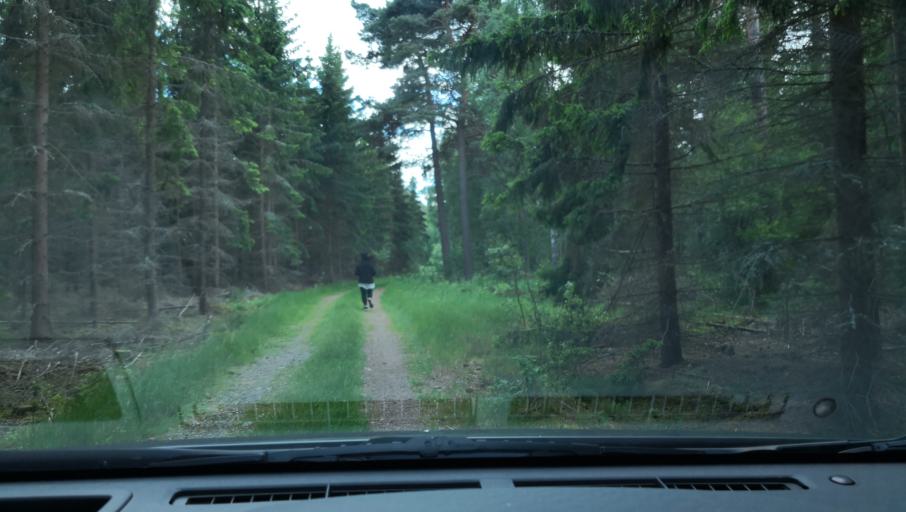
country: SE
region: OErebro
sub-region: Lindesbergs Kommun
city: Fellingsbro
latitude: 59.3051
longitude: 15.6680
